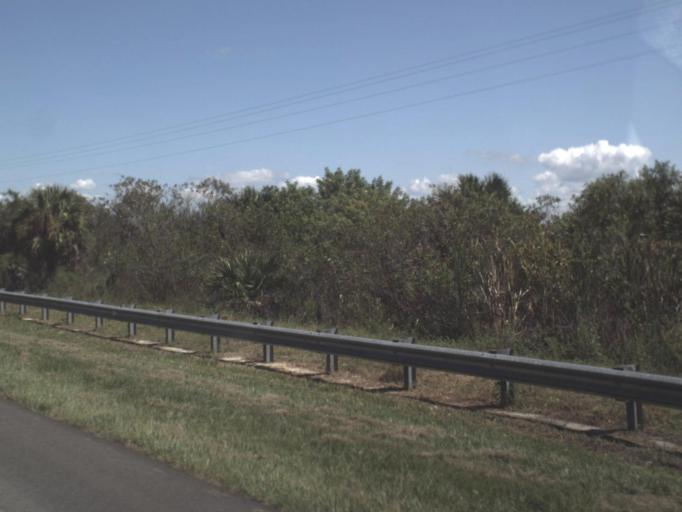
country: US
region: Florida
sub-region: Glades County
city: Buckhead Ridge
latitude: 27.0503
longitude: -80.9867
